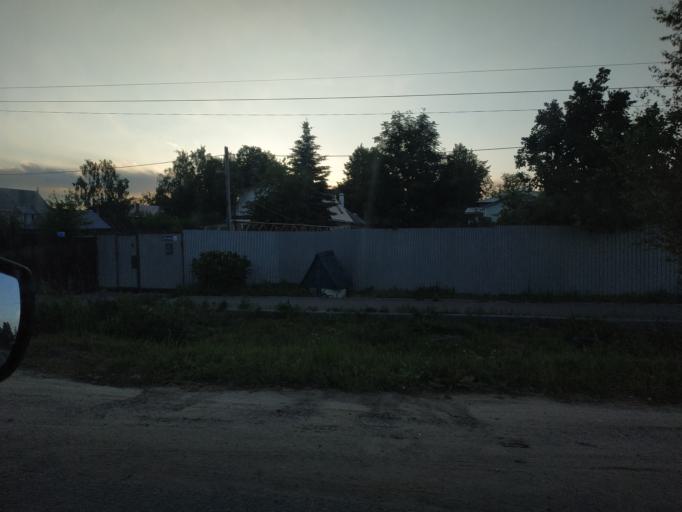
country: RU
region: Moskovskaya
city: Chernogolovka
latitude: 56.0628
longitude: 38.2572
